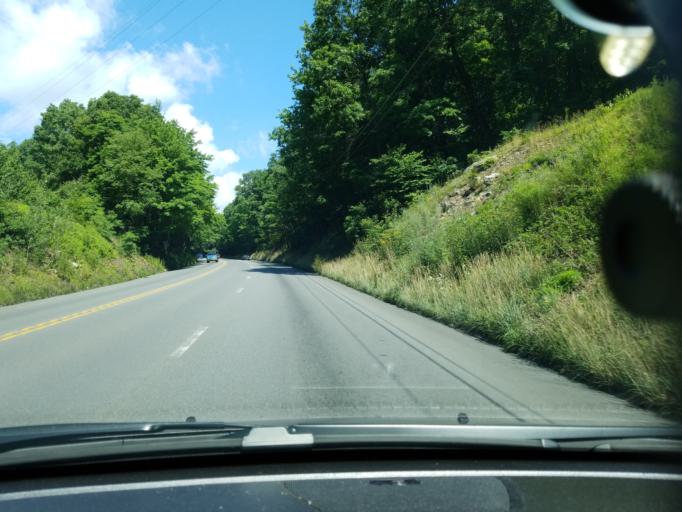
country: US
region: Pennsylvania
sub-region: Northumberland County
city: Mount Carmel
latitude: 40.8073
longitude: -76.4421
